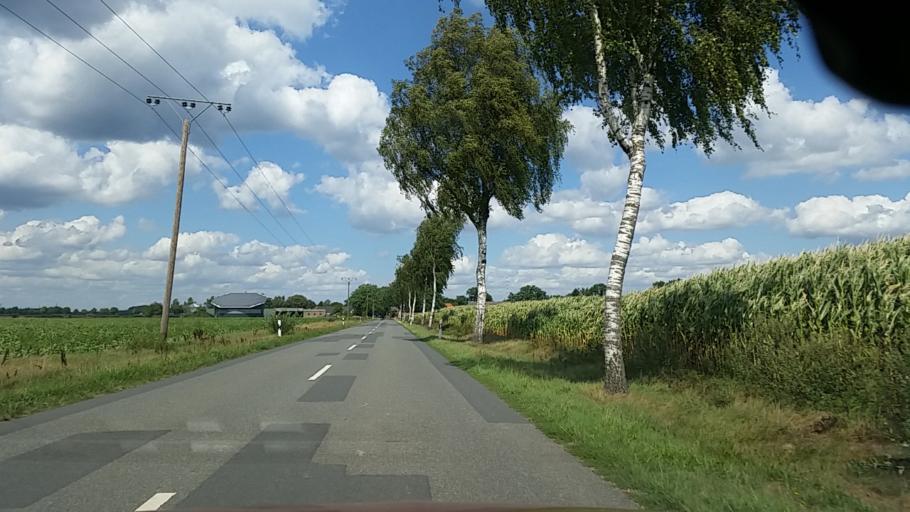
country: DE
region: Lower Saxony
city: Sprakensehl
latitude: 52.7468
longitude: 10.5149
